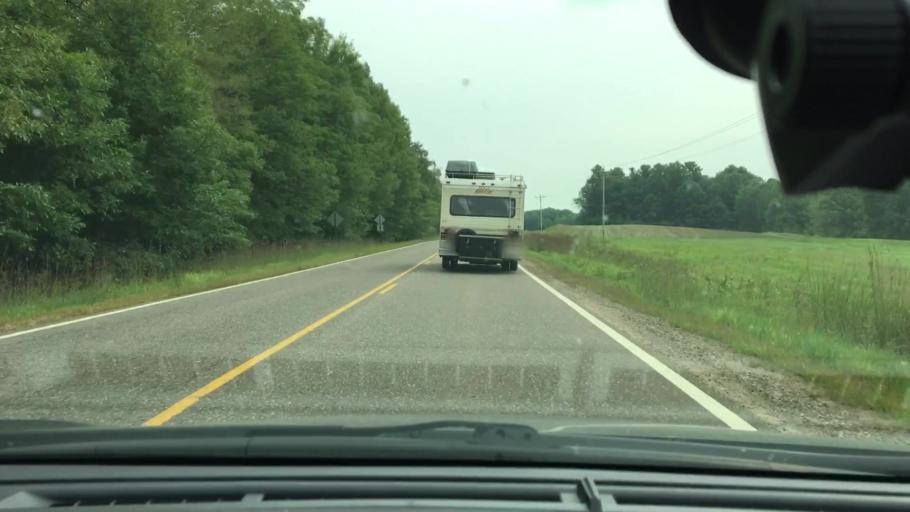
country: US
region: Minnesota
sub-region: Aitkin County
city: Aitkin
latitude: 46.4050
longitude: -93.7890
